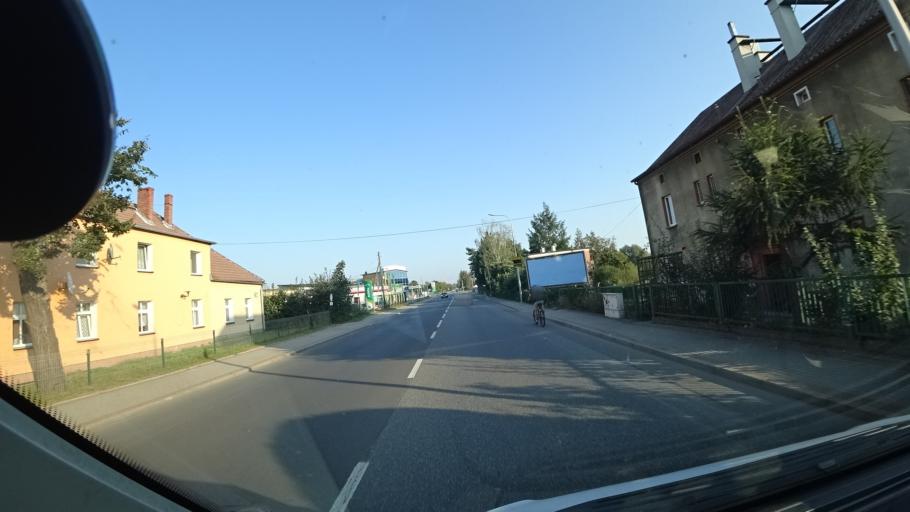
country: PL
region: Opole Voivodeship
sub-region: Powiat kedzierzynsko-kozielski
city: Kozle
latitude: 50.3412
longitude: 18.1747
